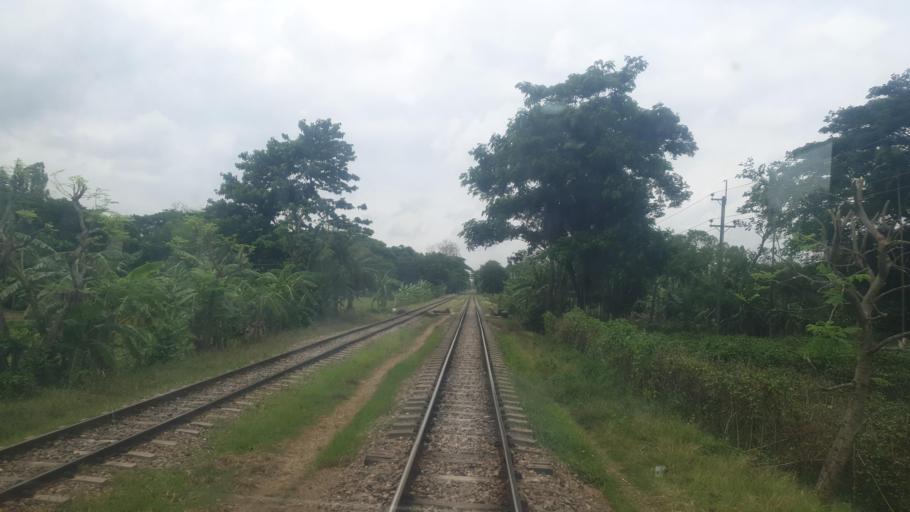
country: BD
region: Chittagong
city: Fatikchari
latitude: 22.6516
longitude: 91.6469
